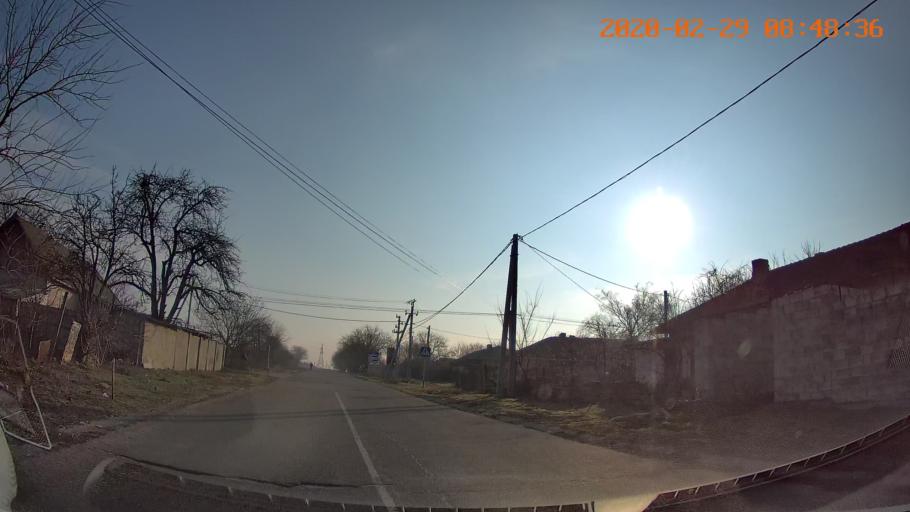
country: MD
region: Anenii Noi
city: Varnita
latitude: 46.9200
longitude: 29.4847
